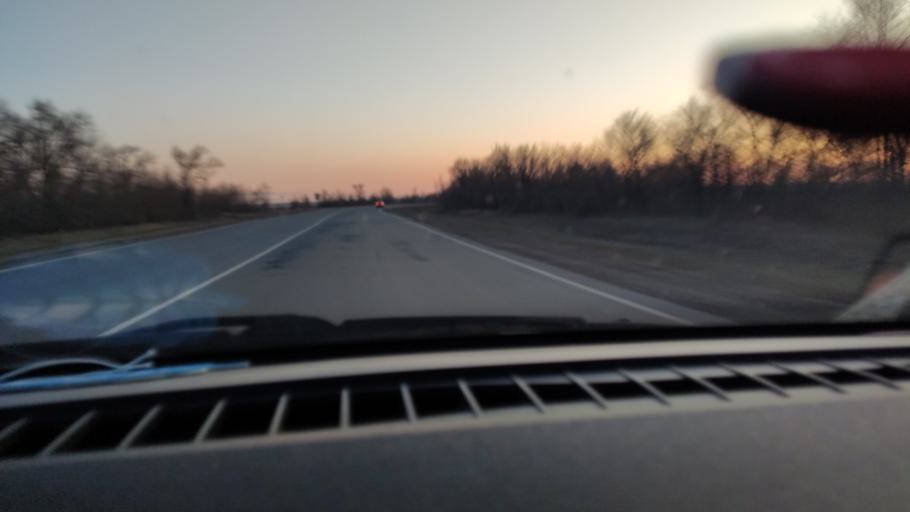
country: RU
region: Saratov
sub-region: Saratovskiy Rayon
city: Saratov
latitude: 51.7064
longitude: 46.0144
